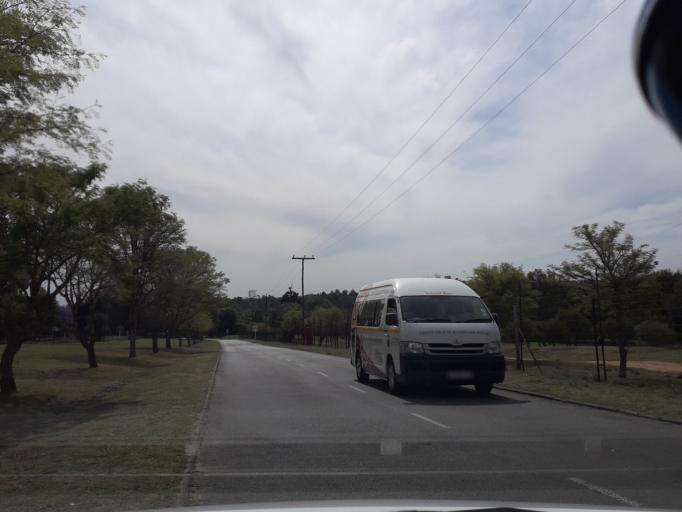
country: ZA
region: Gauteng
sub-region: City of Johannesburg Metropolitan Municipality
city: Diepsloot
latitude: -25.9785
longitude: 28.0558
